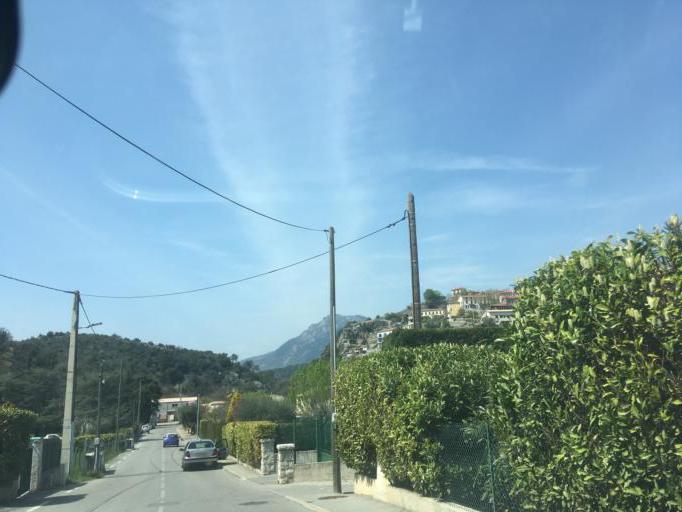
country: FR
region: Provence-Alpes-Cote d'Azur
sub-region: Departement des Alpes-Maritimes
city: Levens
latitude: 43.8550
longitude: 7.2294
